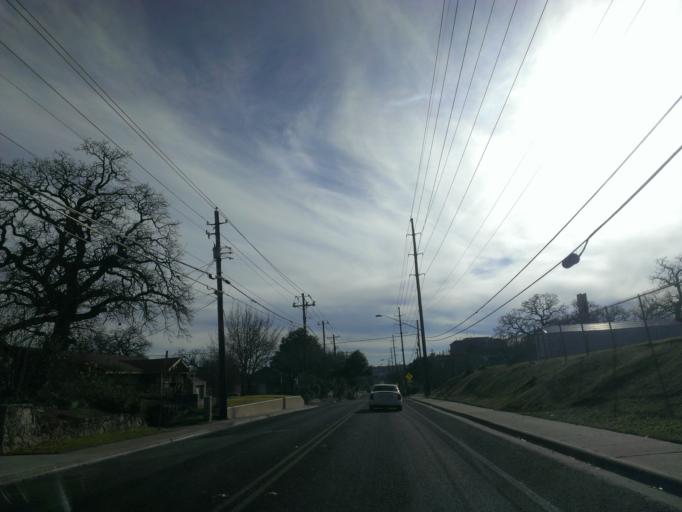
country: US
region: Texas
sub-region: Travis County
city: Austin
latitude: 30.2657
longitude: -97.7207
